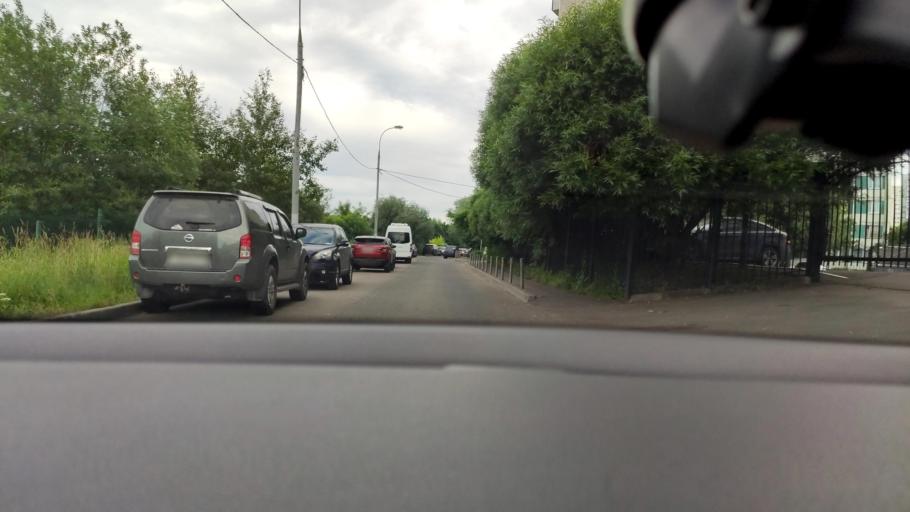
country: RU
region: Moscow
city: Shchukino
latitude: 55.7650
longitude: 37.4176
